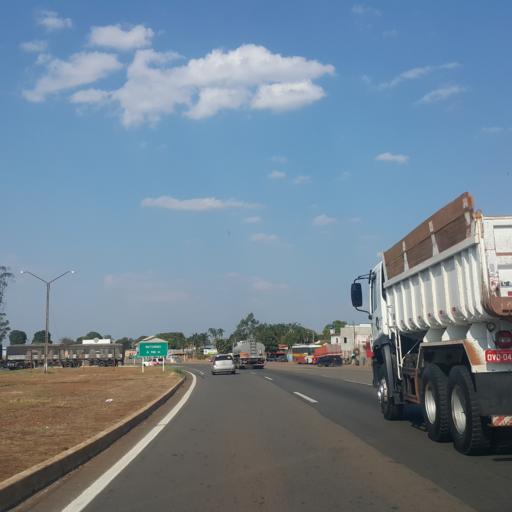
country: BR
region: Goias
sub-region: Abadiania
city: Abadiania
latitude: -16.1916
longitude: -48.7074
